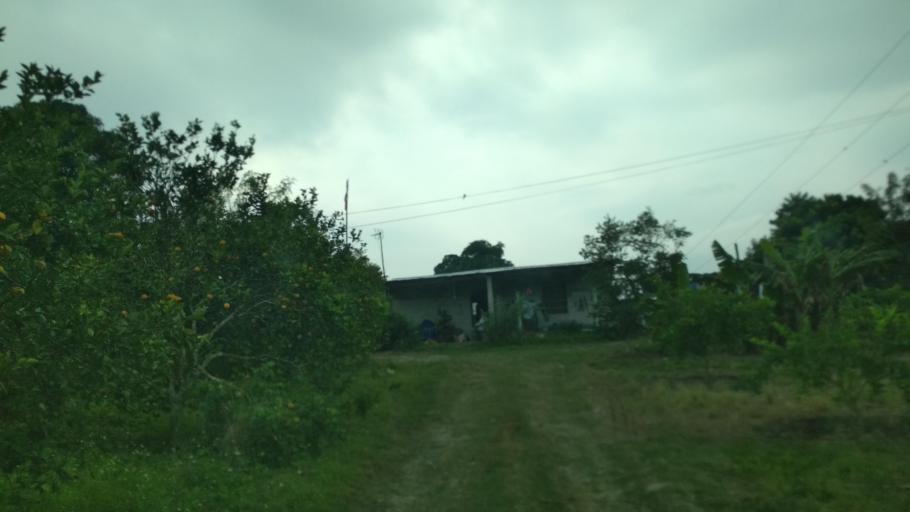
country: MM
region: Kayah
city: Loikaw
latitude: 20.2135
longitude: 97.3287
